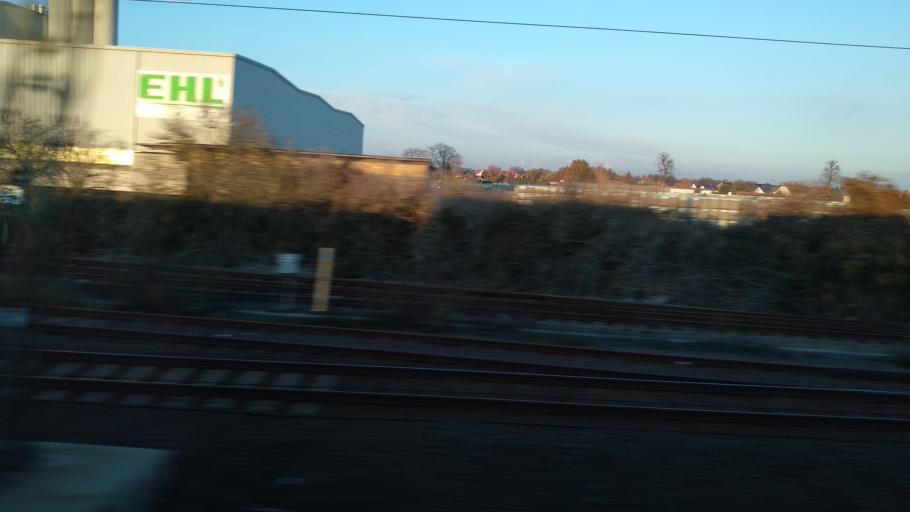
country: DE
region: Saxony
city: Wurzen
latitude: 51.3604
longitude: 12.7564
